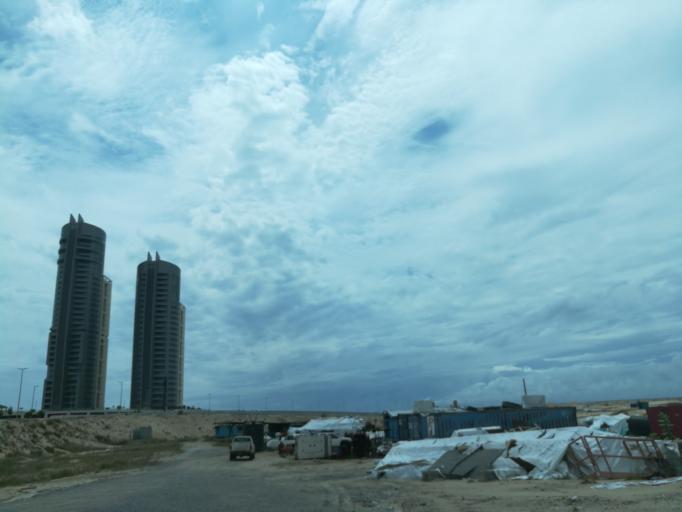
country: NG
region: Lagos
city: Lagos
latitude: 6.4094
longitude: 3.4071
